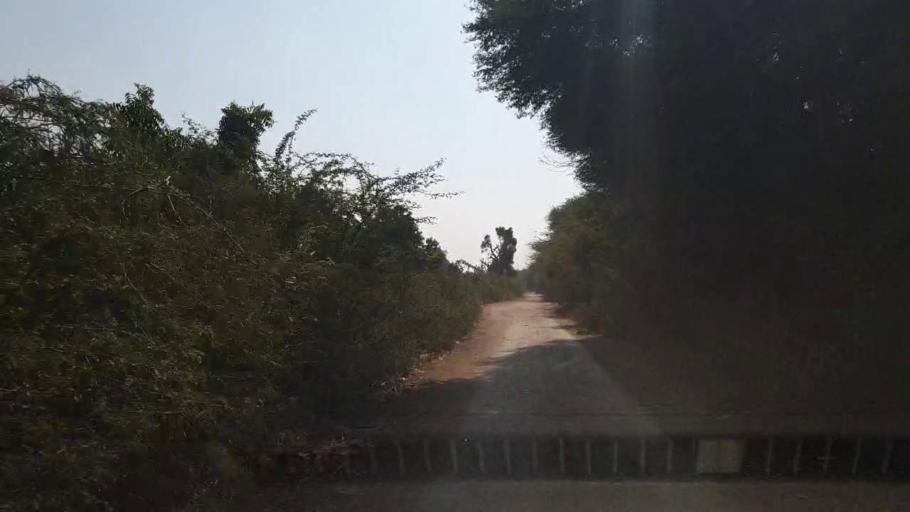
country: PK
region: Sindh
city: Chambar
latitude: 25.3749
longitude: 68.8808
